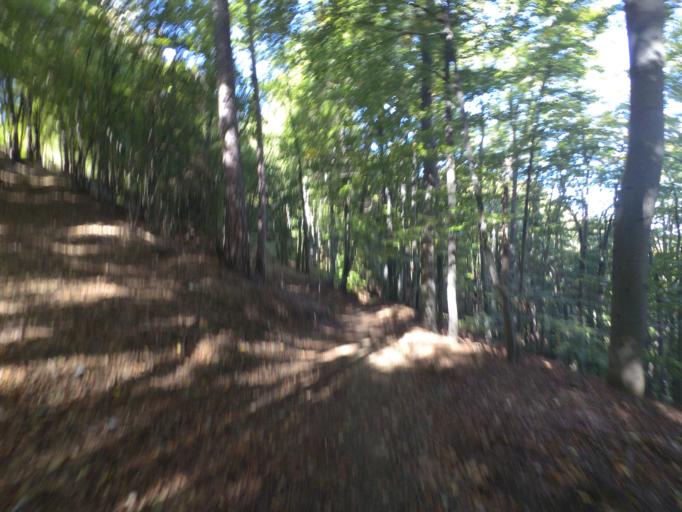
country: AT
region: Styria
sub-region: Politischer Bezirk Leibnitz
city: Kitzeck im Sausal
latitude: 46.7864
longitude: 15.4342
